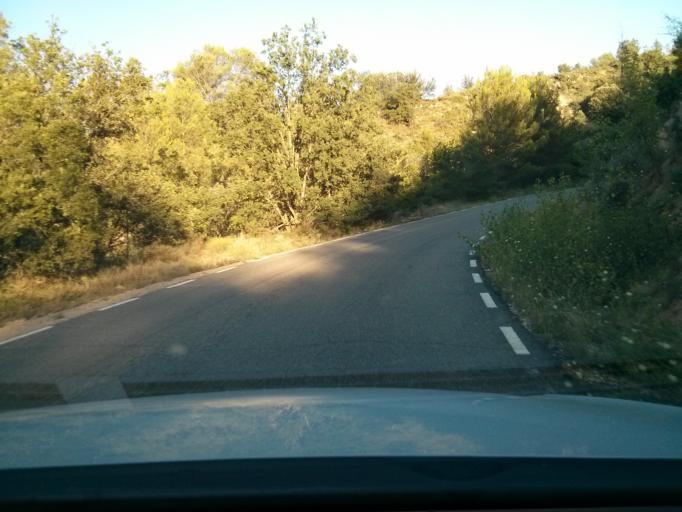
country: ES
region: Castille-La Mancha
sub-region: Provincia de Guadalajara
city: Mantiel
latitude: 40.6338
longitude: -2.6442
